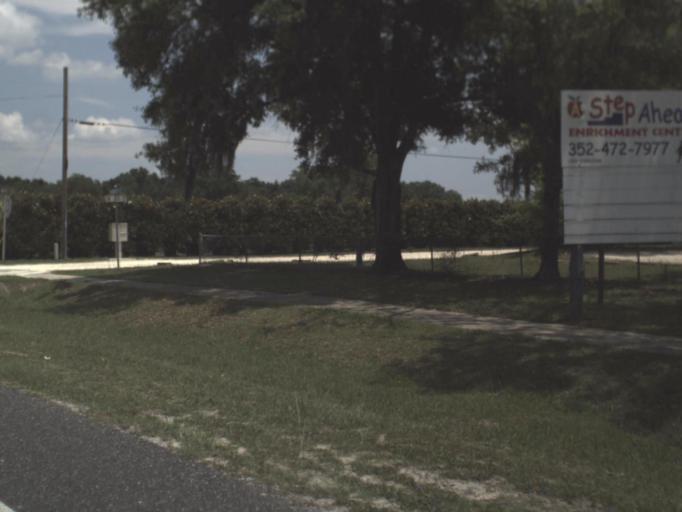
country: US
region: Florida
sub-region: Alachua County
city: Newberry
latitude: 29.6544
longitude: -82.5740
